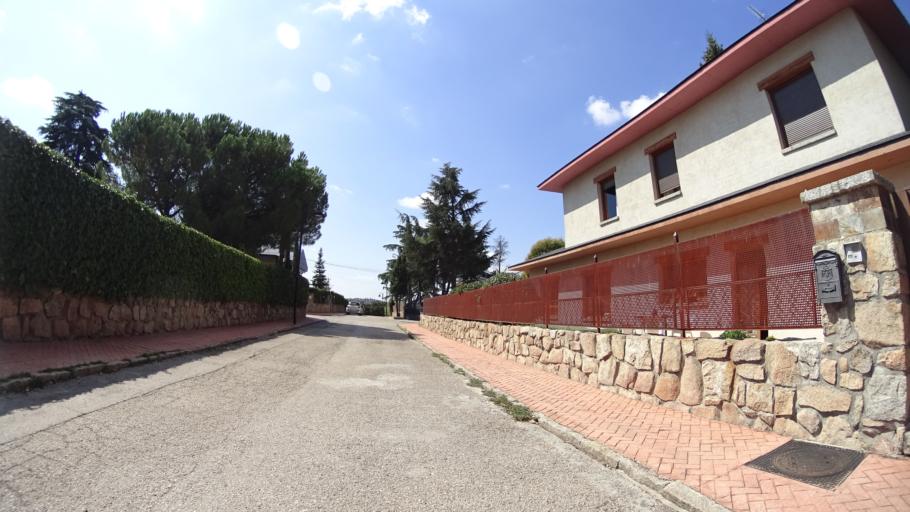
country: ES
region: Madrid
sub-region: Provincia de Madrid
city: Galapagar
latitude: 40.5881
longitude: -3.9939
